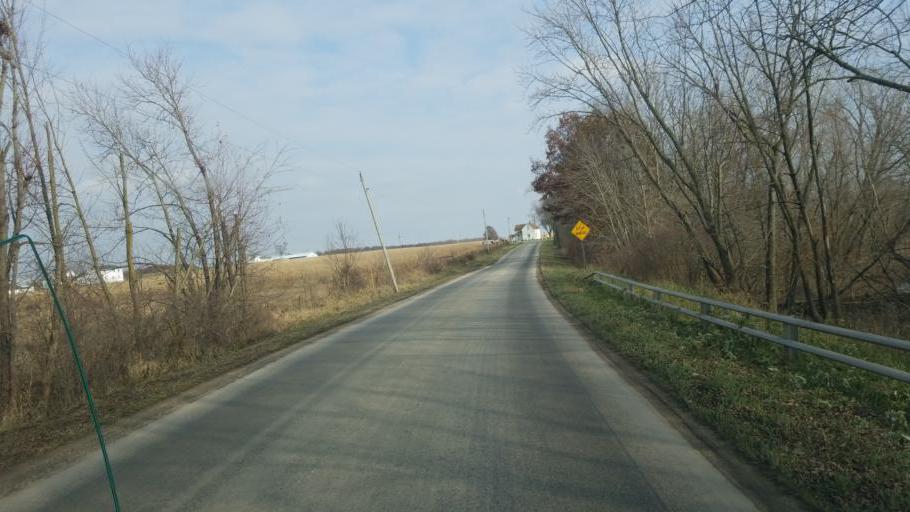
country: US
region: Indiana
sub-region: Adams County
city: Geneva
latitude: 40.6157
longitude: -84.9388
